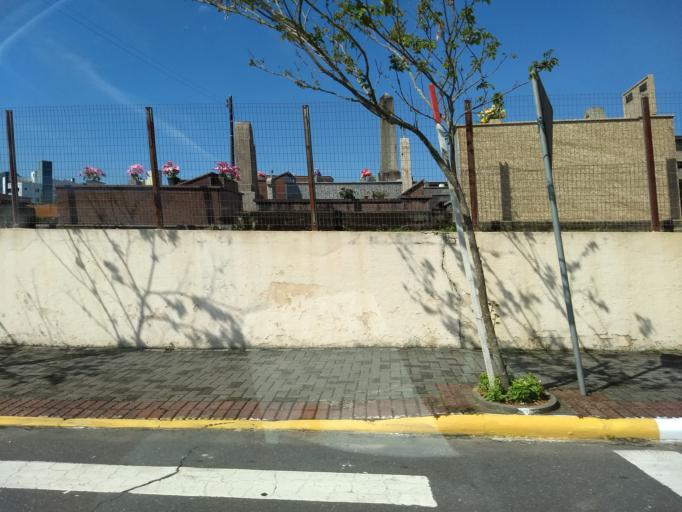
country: BR
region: Santa Catarina
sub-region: Jaragua Do Sul
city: Jaragua do Sul
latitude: -26.4881
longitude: -49.0759
